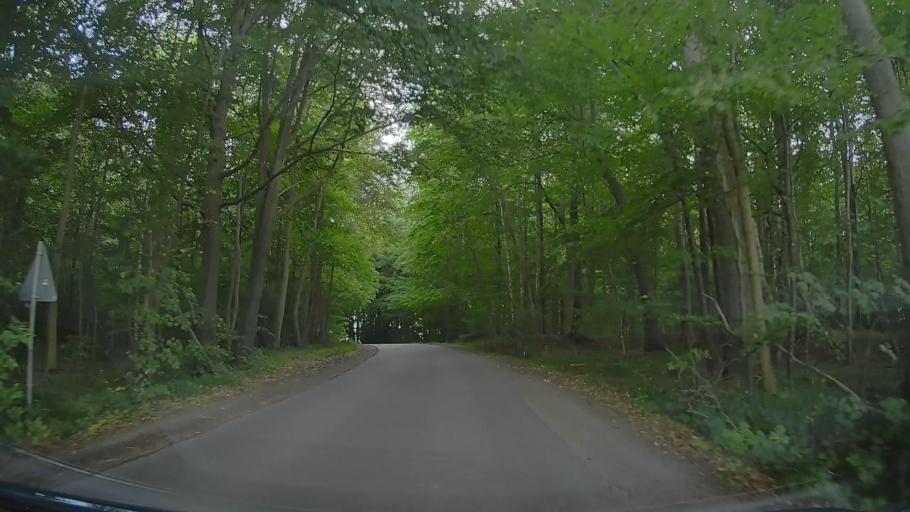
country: DE
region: Schleswig-Holstein
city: Steinberg
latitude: 54.7867
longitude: 9.7794
